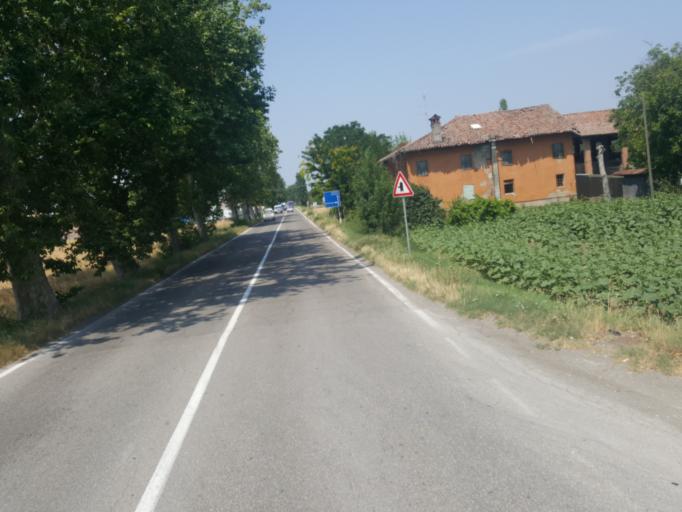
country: IT
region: Emilia-Romagna
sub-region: Provincia di Bologna
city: Calcara
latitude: 44.5543
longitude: 11.1694
